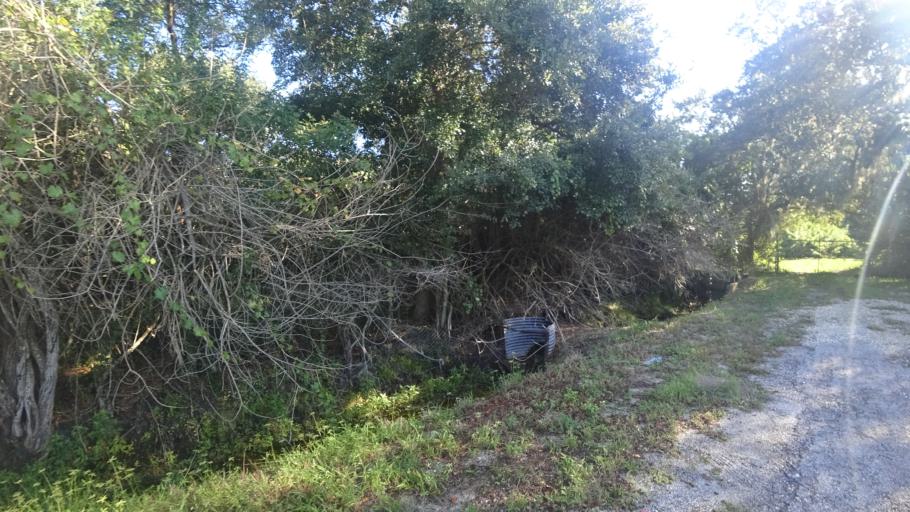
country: US
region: Florida
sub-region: Manatee County
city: Memphis
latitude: 27.5941
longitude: -82.5195
